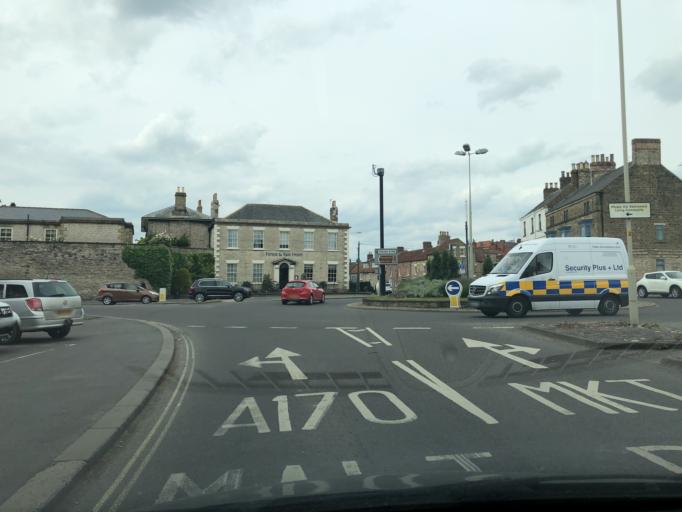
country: GB
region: England
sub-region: North Yorkshire
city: Pickering
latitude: 54.2438
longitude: -0.7747
